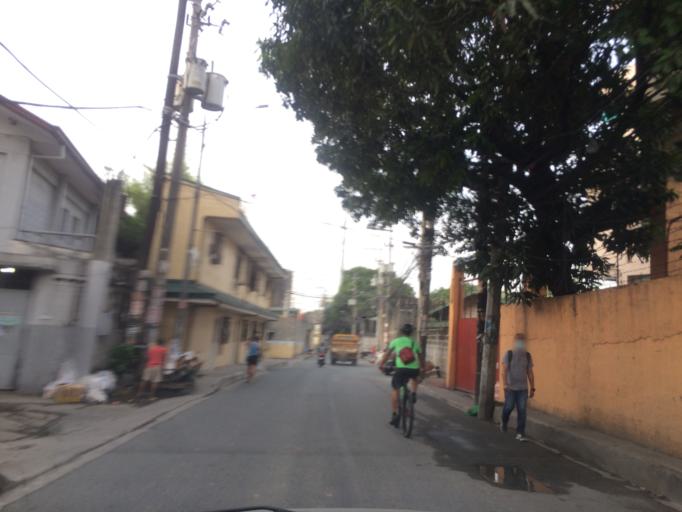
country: PH
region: Calabarzon
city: Del Monte
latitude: 14.6533
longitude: 121.0103
